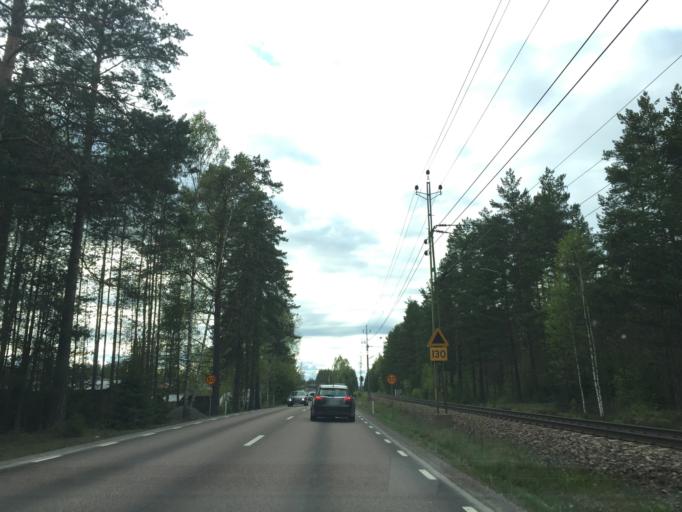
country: SE
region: Vaermland
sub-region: Eda Kommun
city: Charlottenberg
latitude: 59.9249
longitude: 12.2580
